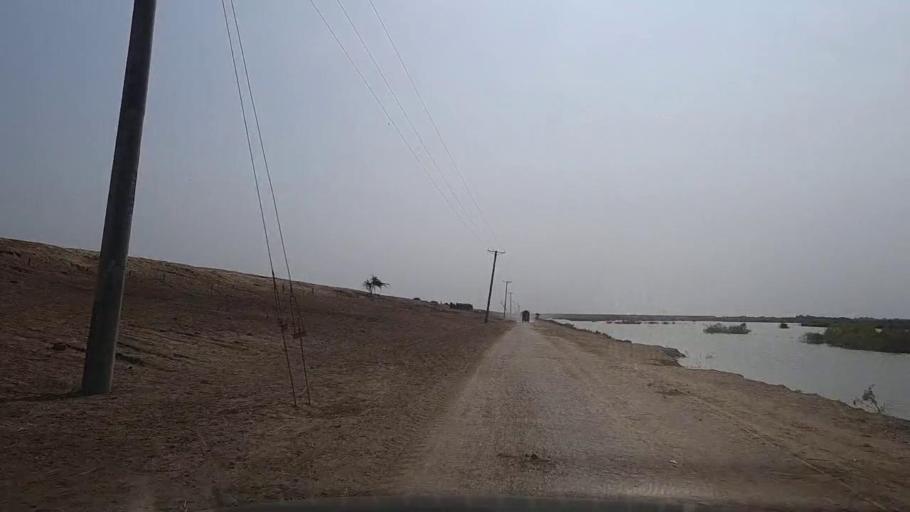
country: PK
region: Sindh
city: Thatta
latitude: 24.5816
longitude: 67.9150
